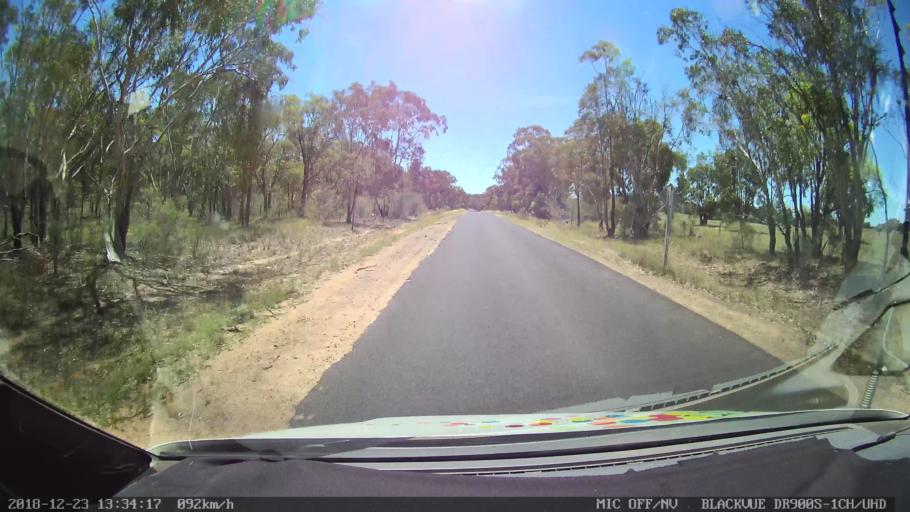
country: AU
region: New South Wales
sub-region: Armidale Dumaresq
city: Armidale
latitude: -30.4511
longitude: 151.2667
